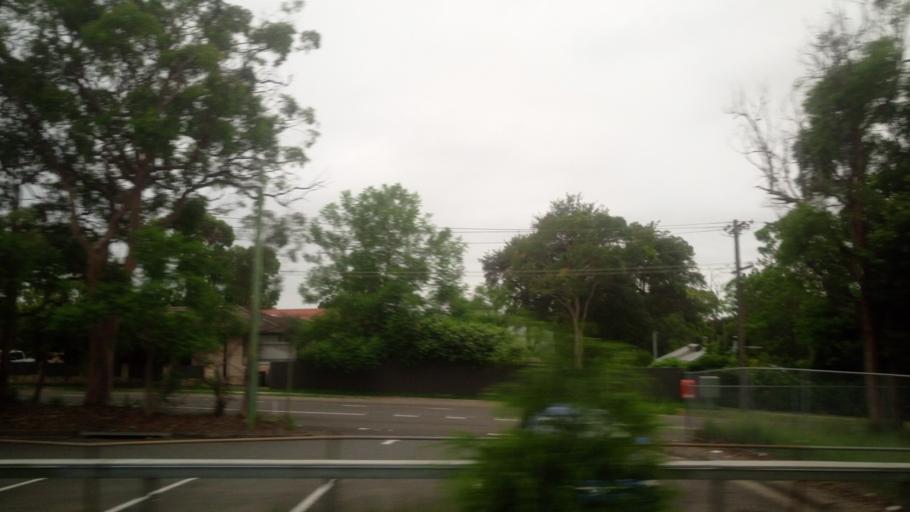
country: AU
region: New South Wales
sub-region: Blue Mountains Municipality
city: Blaxland
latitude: -33.7219
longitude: 150.6039
